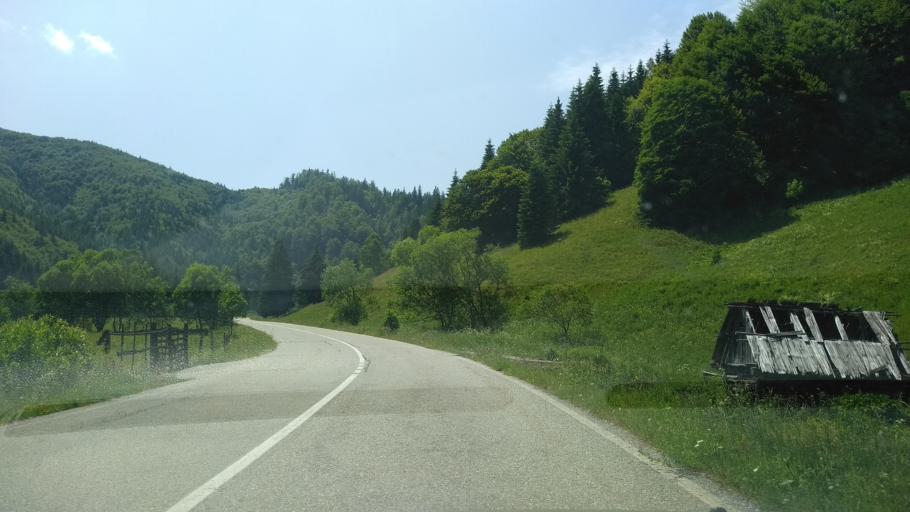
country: RO
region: Hunedoara
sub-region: Comuna Rau de Mori
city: Rau de Mori
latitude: 45.2793
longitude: 22.9240
